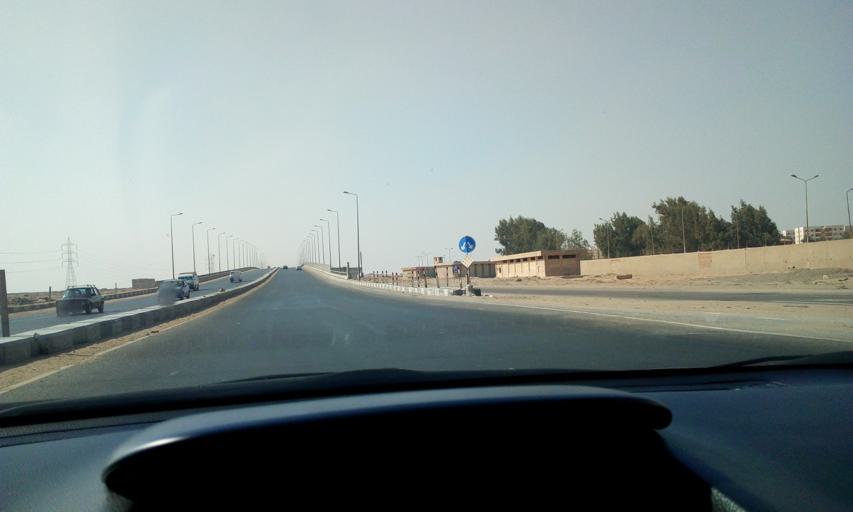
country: EG
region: Al Jizah
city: Madinat Sittah Uktubar
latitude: 29.8790
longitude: 31.0770
